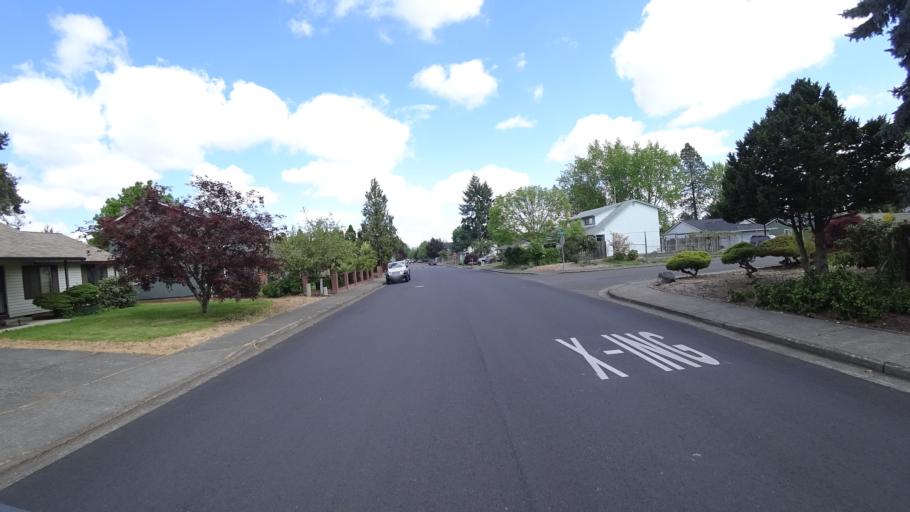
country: US
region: Oregon
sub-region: Washington County
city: Aloha
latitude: 45.5066
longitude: -122.8943
